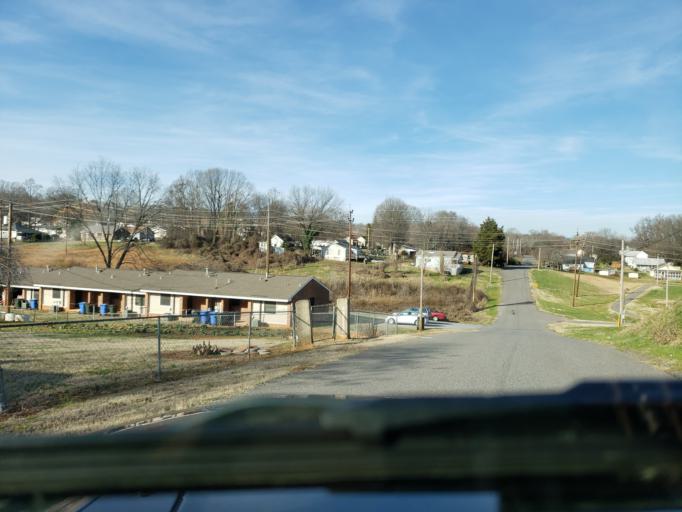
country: US
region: North Carolina
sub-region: Cleveland County
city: Kings Mountain
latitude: 35.2443
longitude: -81.3348
